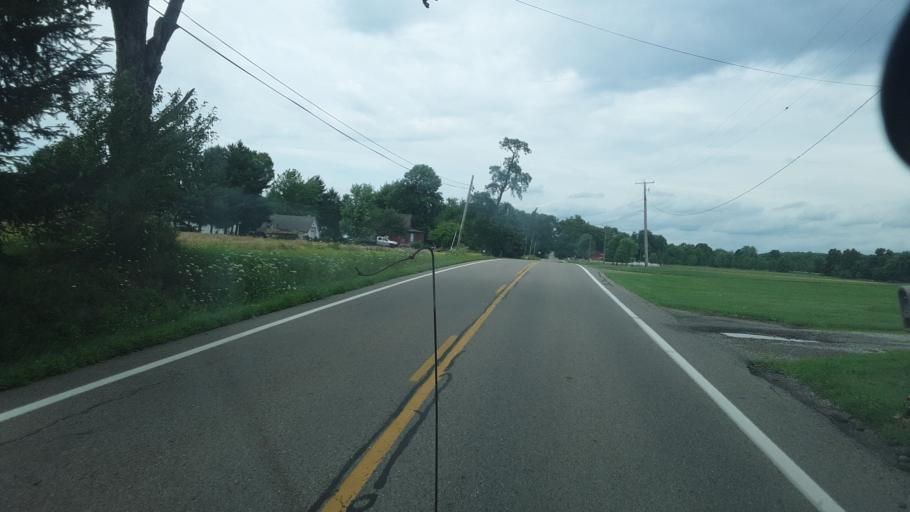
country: US
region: Ohio
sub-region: Trumbull County
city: Cortland
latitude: 41.4410
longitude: -80.6655
